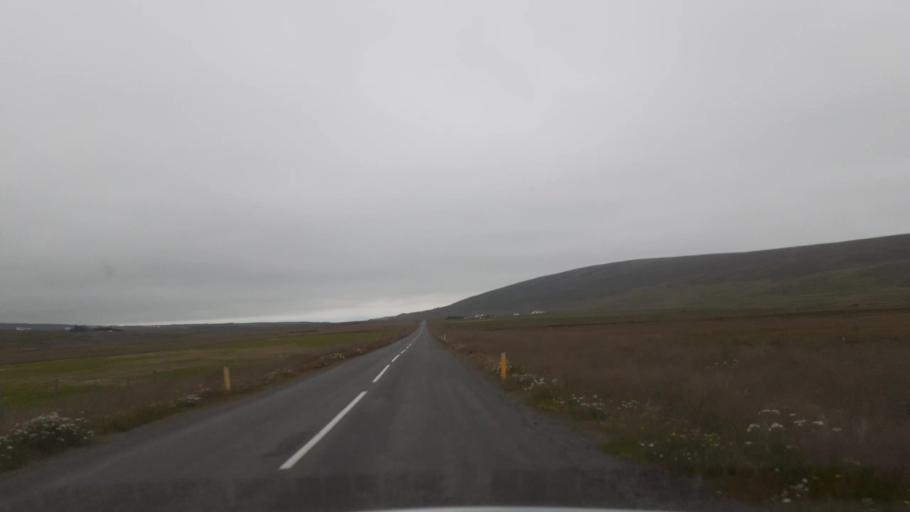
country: IS
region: Northeast
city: Siglufjoerdur
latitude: 65.7420
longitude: -19.1460
